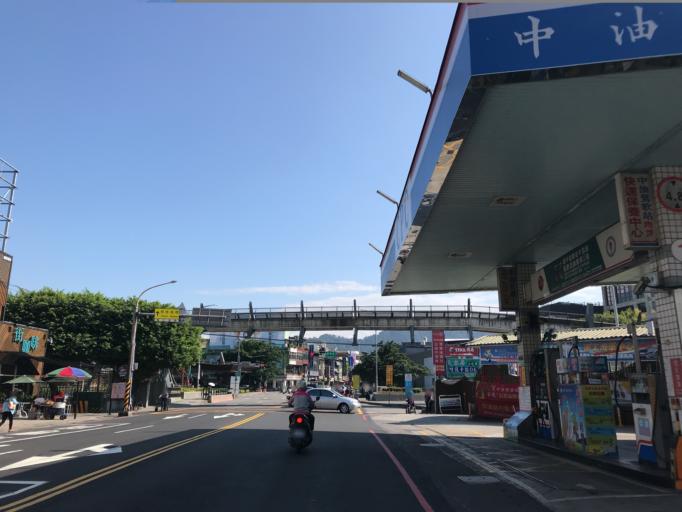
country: TW
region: Taiwan
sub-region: Taoyuan
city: Taoyuan
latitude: 24.9505
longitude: 121.3523
